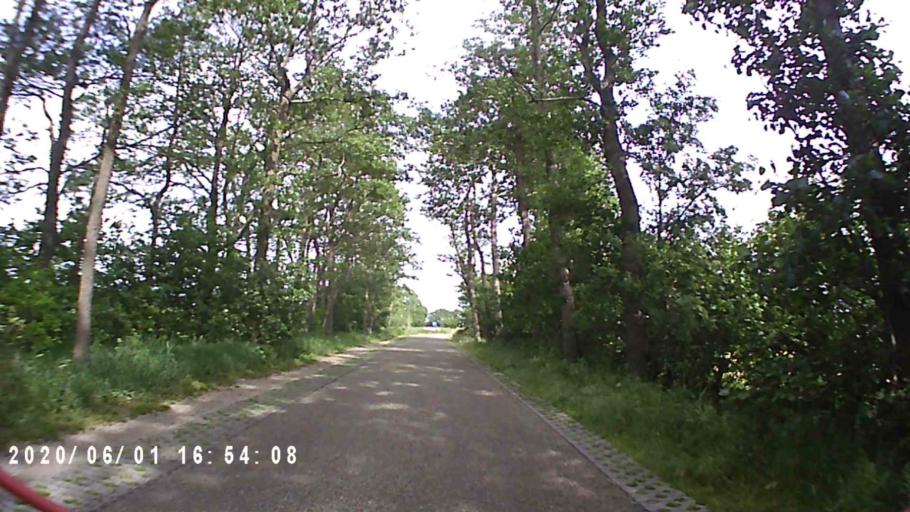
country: NL
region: Friesland
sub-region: Gemeente Tytsjerksteradiel
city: Tytsjerk
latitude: 53.1896
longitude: 5.9246
